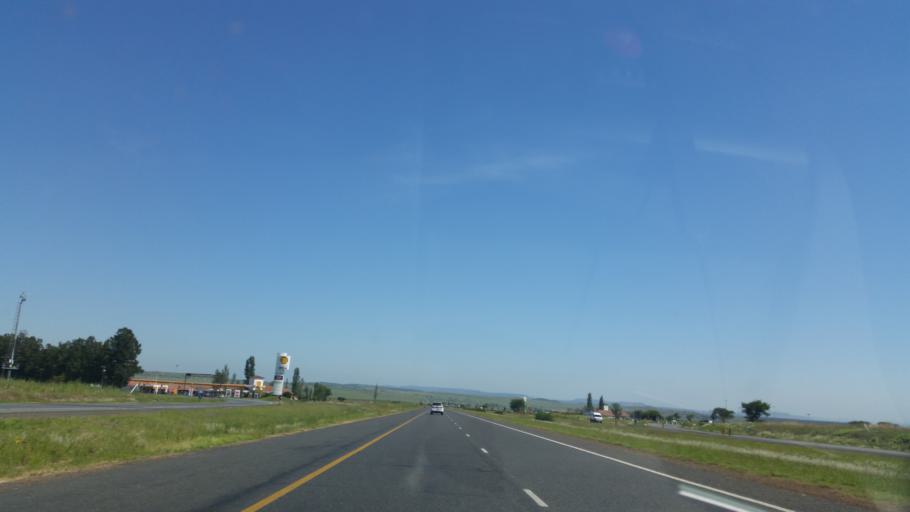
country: ZA
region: KwaZulu-Natal
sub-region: uThukela District Municipality
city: Estcourt
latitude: -28.9282
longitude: 29.7826
